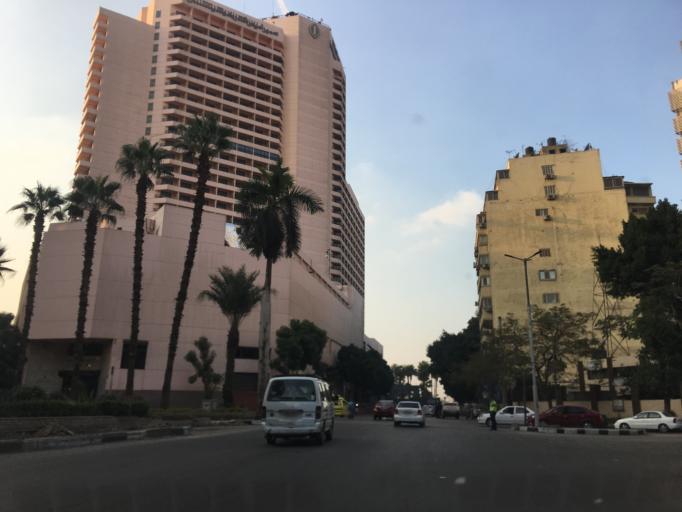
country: EG
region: Muhafazat al Qahirah
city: Cairo
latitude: 30.0421
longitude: 31.2335
